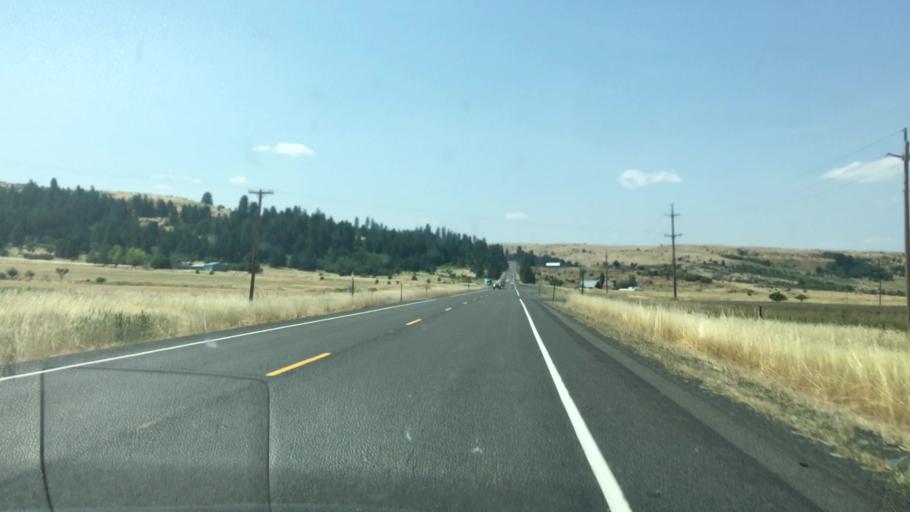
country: US
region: Idaho
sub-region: Idaho County
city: Grangeville
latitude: 45.8819
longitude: -116.2144
